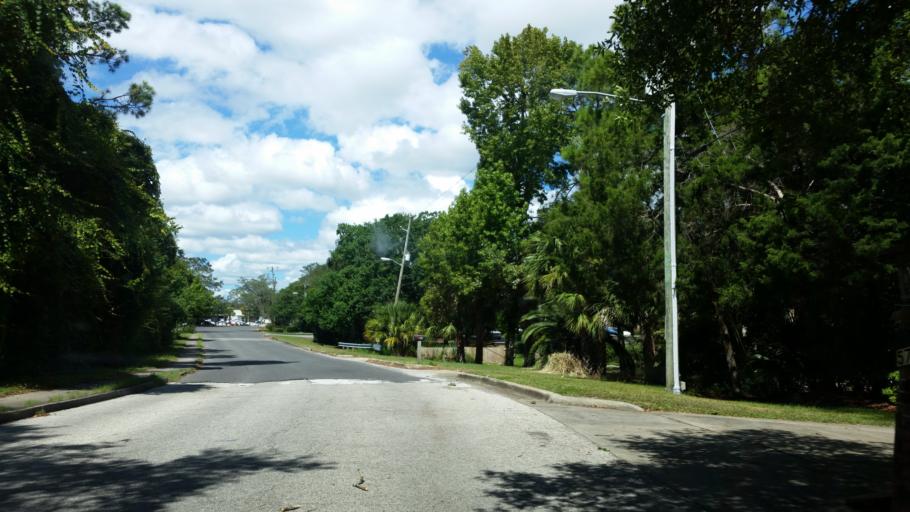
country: US
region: Florida
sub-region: Okaloosa County
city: Ocean City
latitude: 30.4232
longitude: -86.6067
